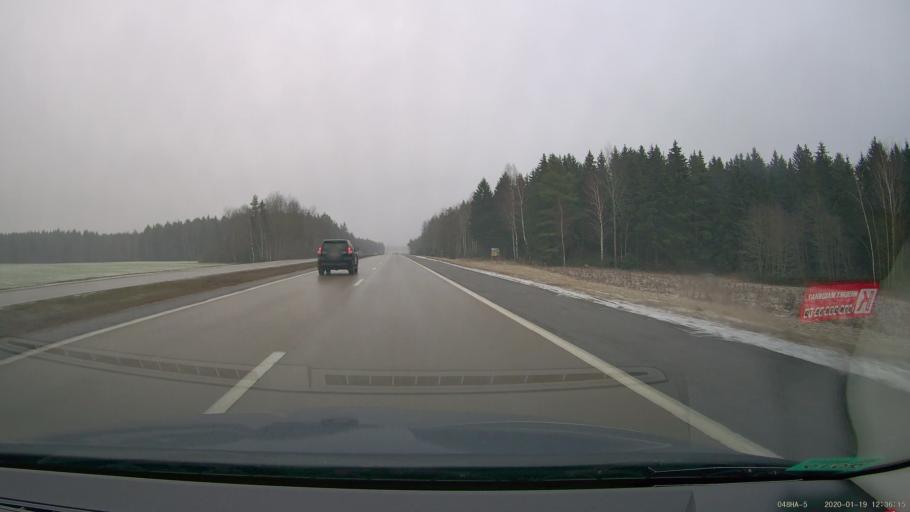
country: BY
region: Minsk
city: Astrashytski Haradok
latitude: 54.0856
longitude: 27.7574
